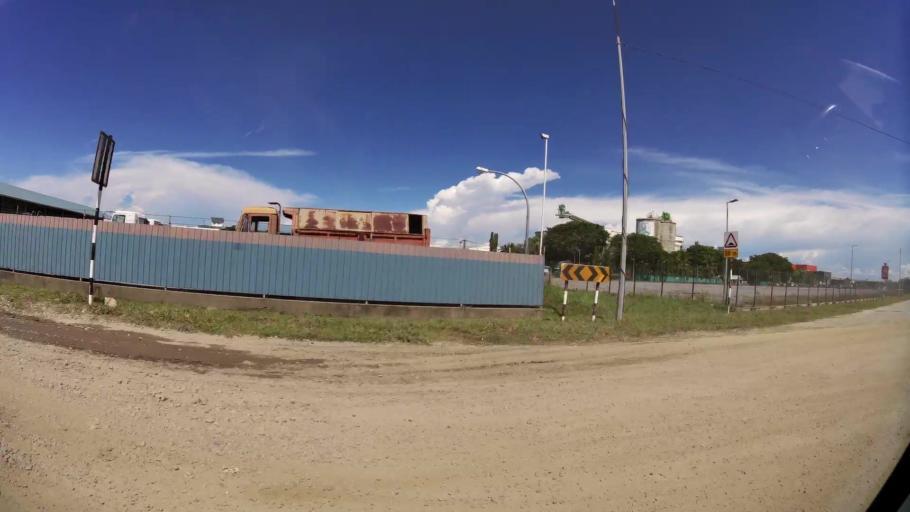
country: BN
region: Brunei and Muara
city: Bandar Seri Begawan
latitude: 5.0145
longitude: 115.0630
